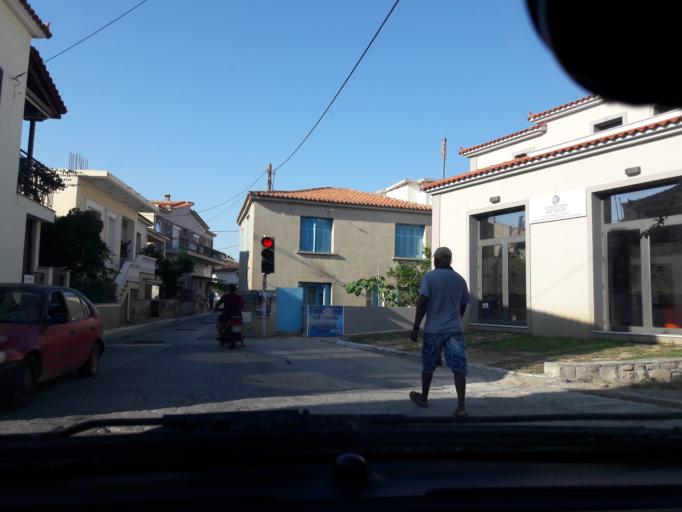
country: GR
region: North Aegean
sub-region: Nomos Lesvou
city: Myrina
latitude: 39.8737
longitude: 25.0627
